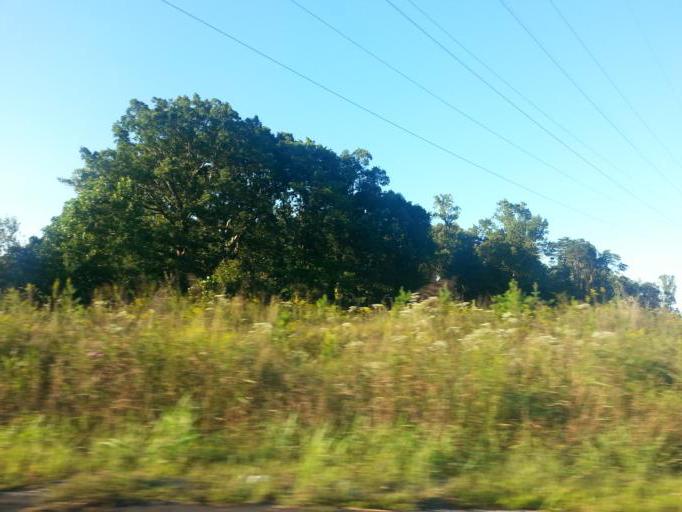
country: US
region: Tennessee
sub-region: Blount County
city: Alcoa
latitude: 35.8444
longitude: -83.9872
